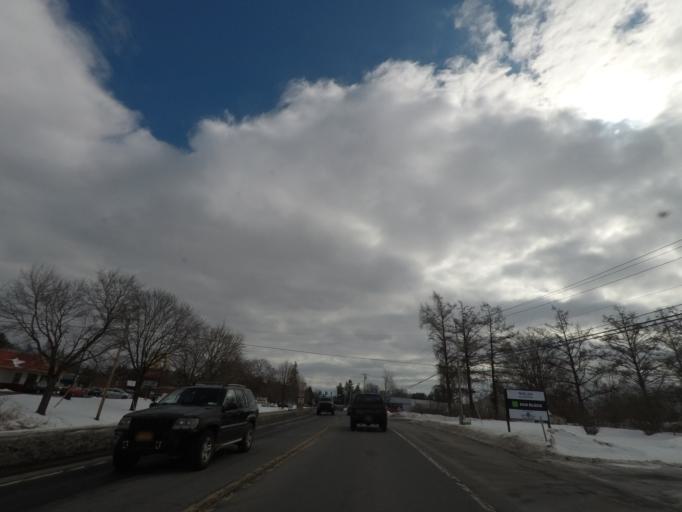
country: US
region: New York
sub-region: Washington County
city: Greenwich
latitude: 43.0980
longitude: -73.5113
